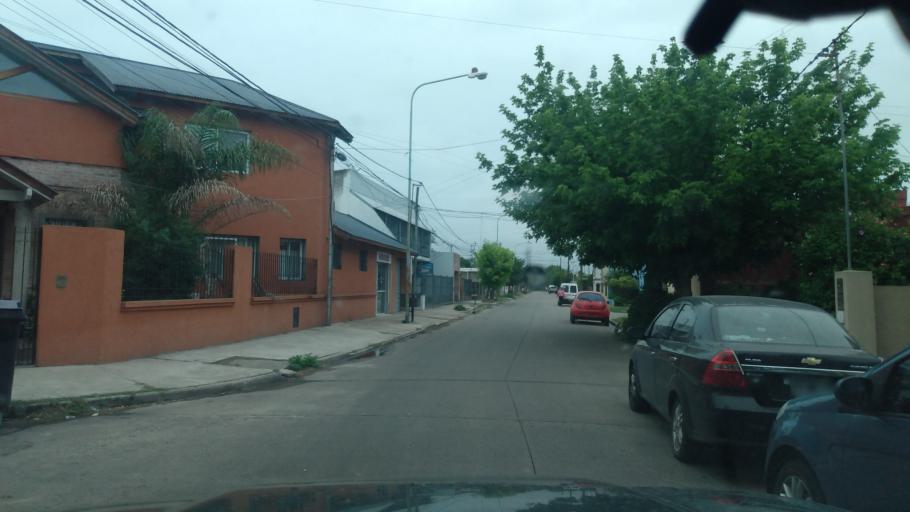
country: AR
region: Buenos Aires
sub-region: Partido de Lujan
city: Lujan
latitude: -34.5747
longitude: -59.1179
